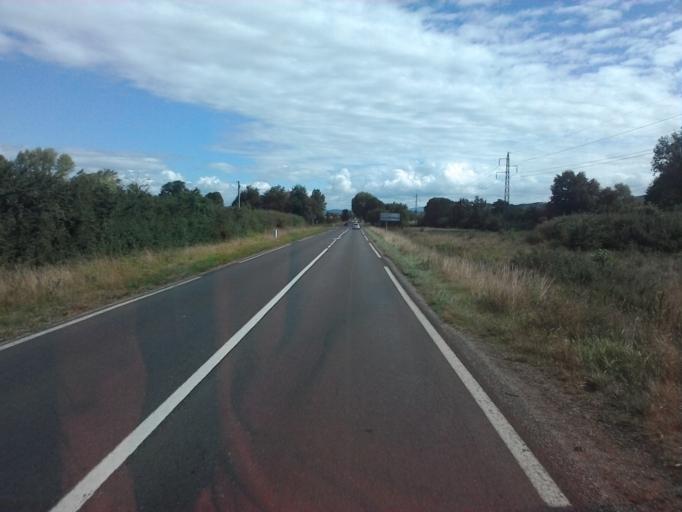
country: FR
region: Rhone-Alpes
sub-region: Departement de l'Ain
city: Ambronay
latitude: 45.9847
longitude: 5.3486
